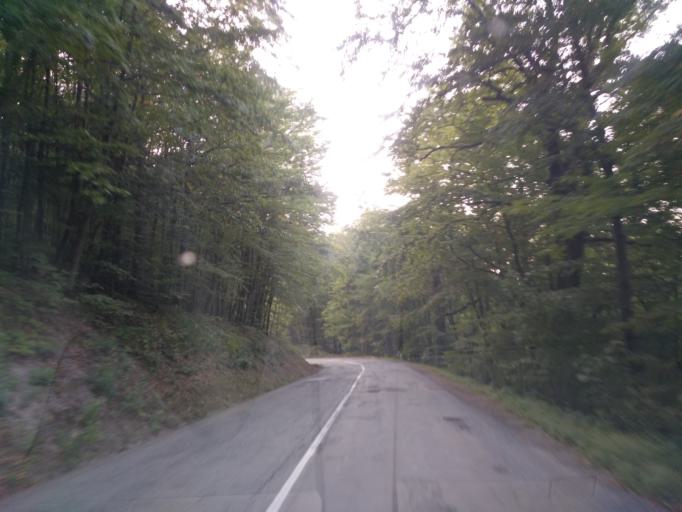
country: SK
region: Kosicky
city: Kosice
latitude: 48.7474
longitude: 21.2055
